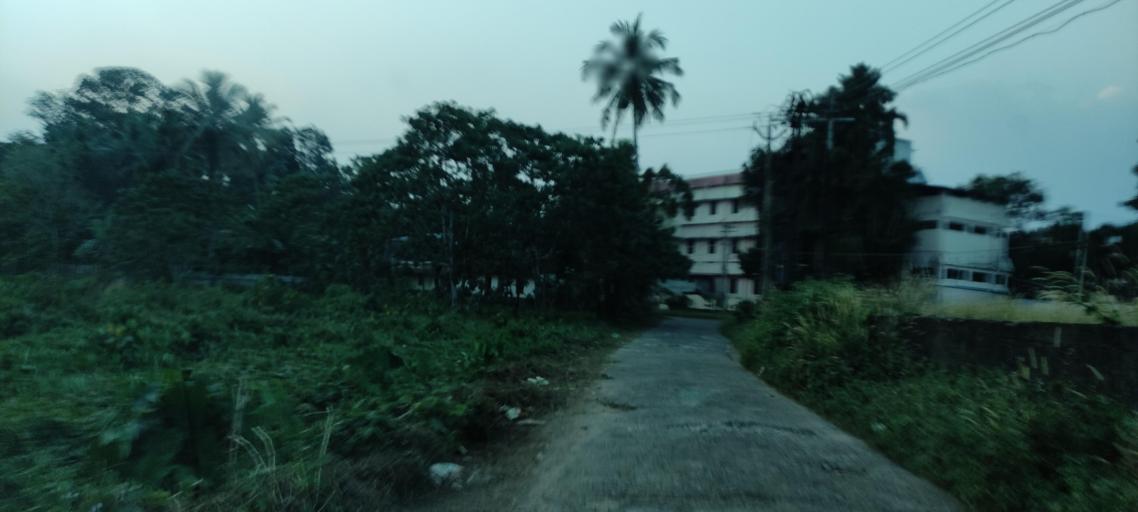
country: IN
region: Kerala
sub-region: Pattanamtitta
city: Adur
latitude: 9.1577
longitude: 76.7388
